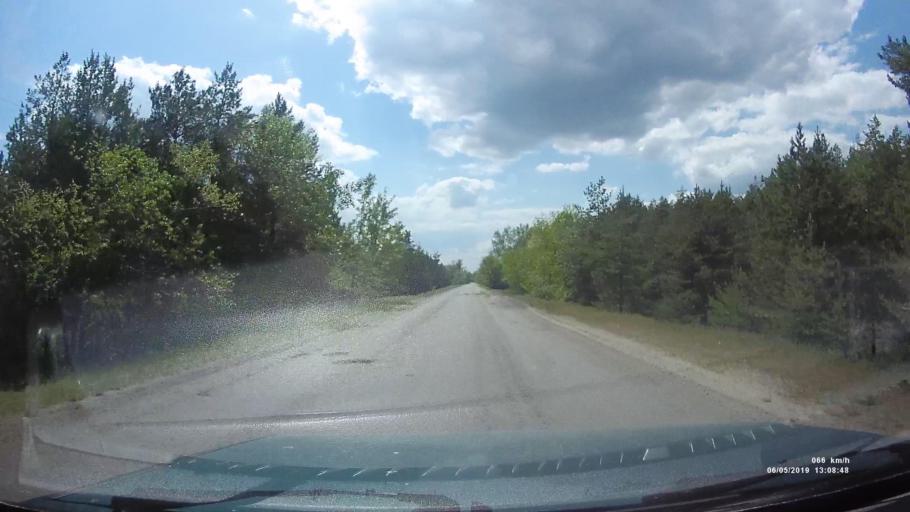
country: RU
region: Rostov
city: Ust'-Donetskiy
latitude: 47.7732
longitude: 40.9915
